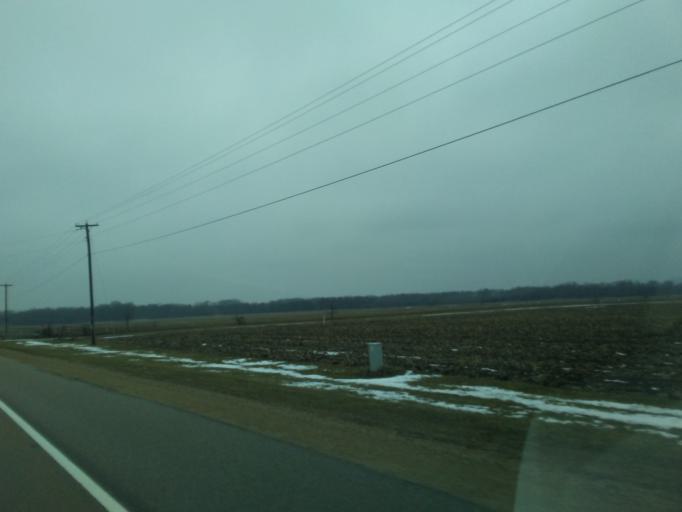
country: US
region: Wisconsin
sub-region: Dane County
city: Mazomanie
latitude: 43.1616
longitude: -89.9212
